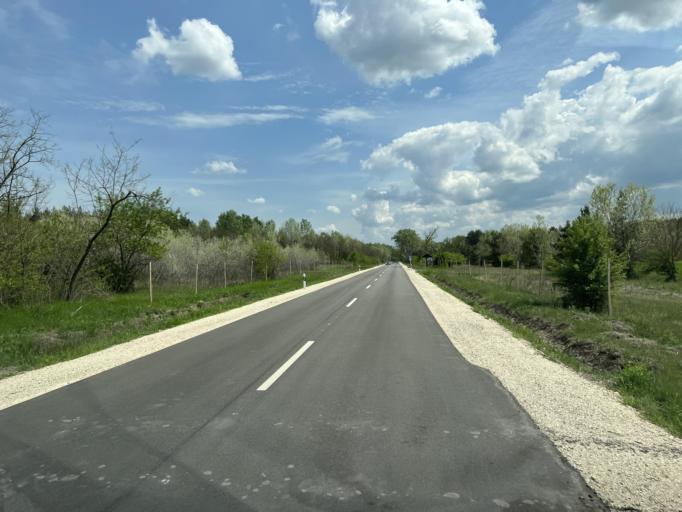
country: HU
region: Pest
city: Csemo
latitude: 47.0878
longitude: 19.6567
